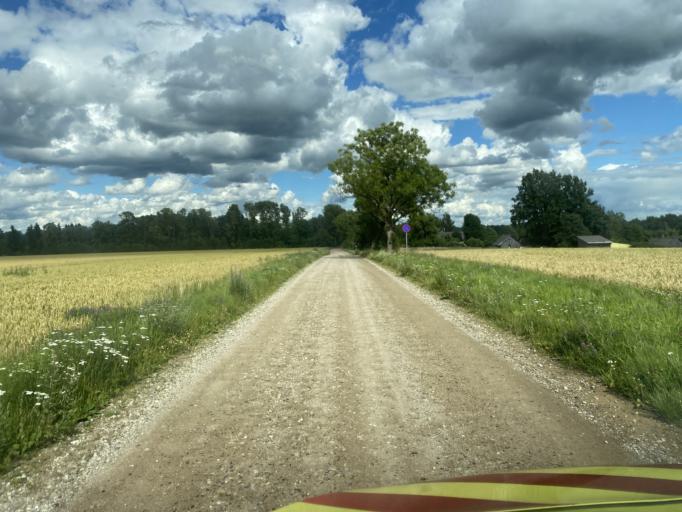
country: EE
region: Viljandimaa
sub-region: Viiratsi vald
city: Viiratsi
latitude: 58.4001
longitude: 25.7831
